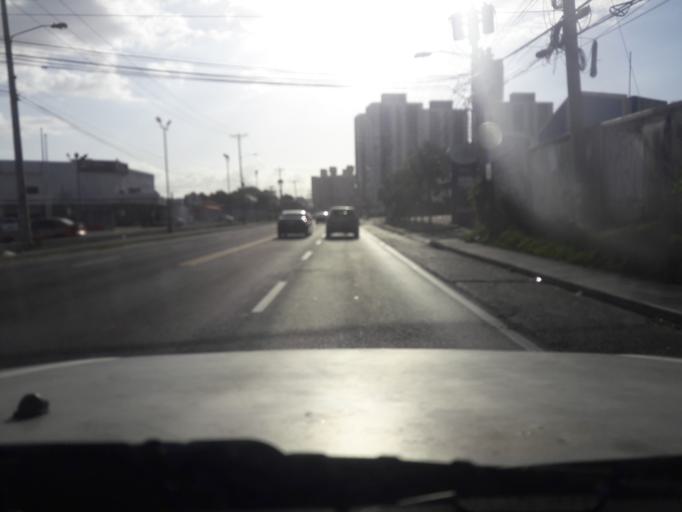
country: PA
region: Panama
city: San Miguelito
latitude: 9.0270
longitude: -79.4821
